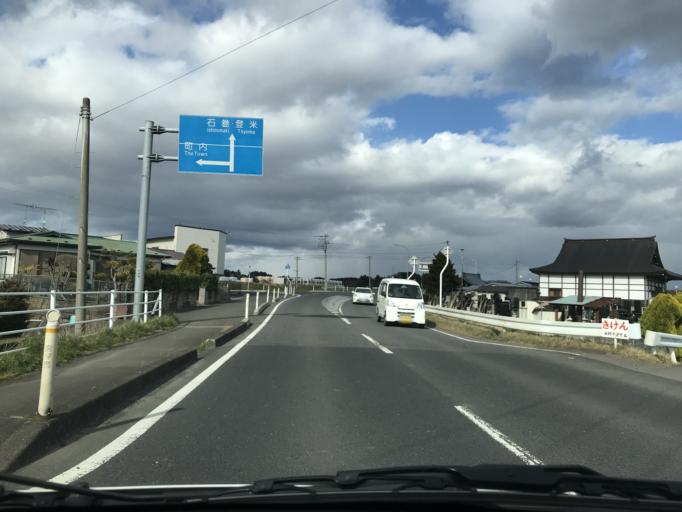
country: JP
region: Miyagi
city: Wakuya
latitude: 38.6262
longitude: 141.2051
